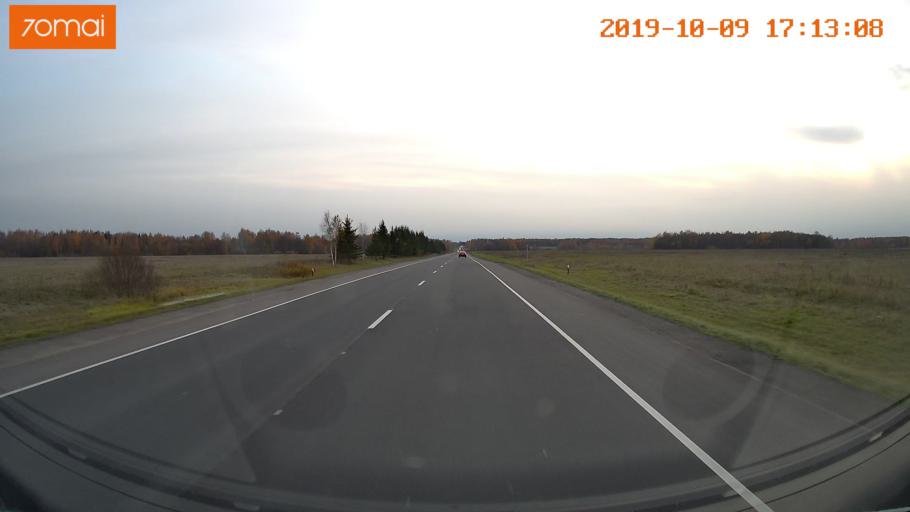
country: RU
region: Ivanovo
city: Privolzhsk
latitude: 57.3190
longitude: 41.2293
